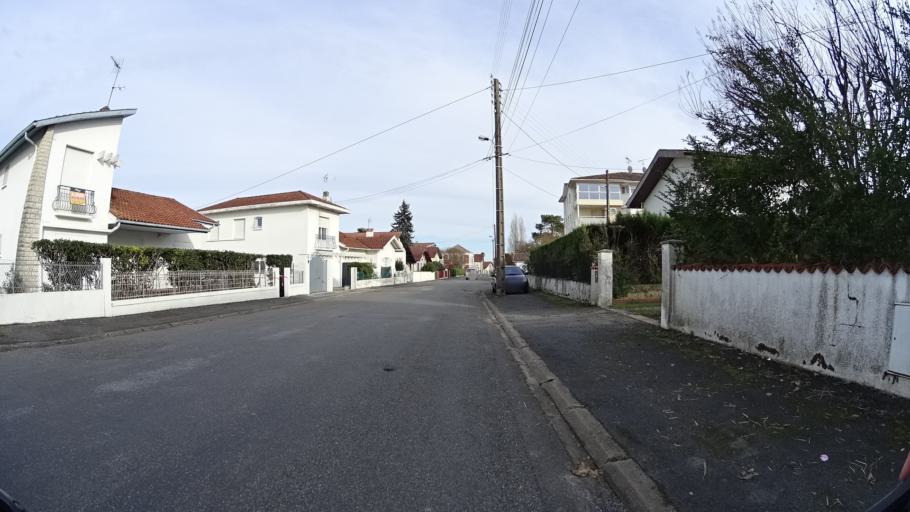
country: FR
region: Aquitaine
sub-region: Departement des Landes
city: Saint-Paul-les-Dax
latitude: 43.7309
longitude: -1.0502
